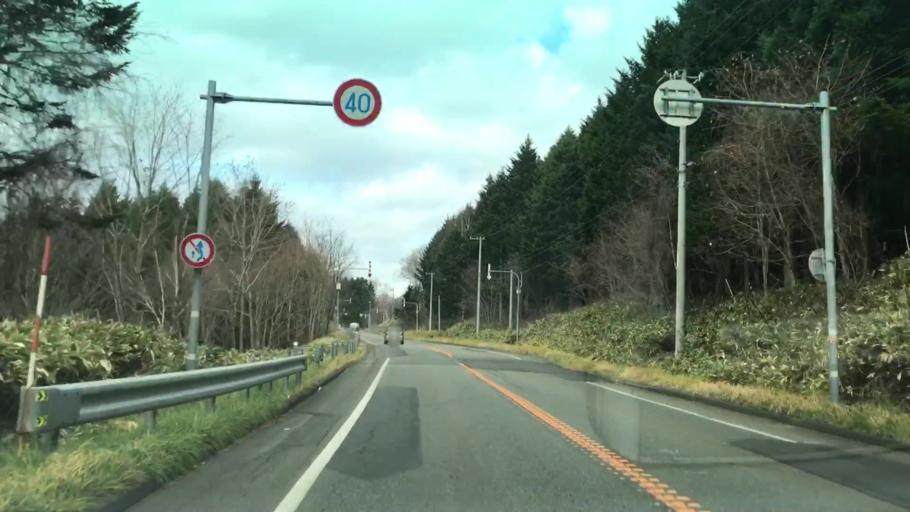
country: JP
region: Hokkaido
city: Shimo-furano
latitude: 42.8956
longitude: 142.4360
